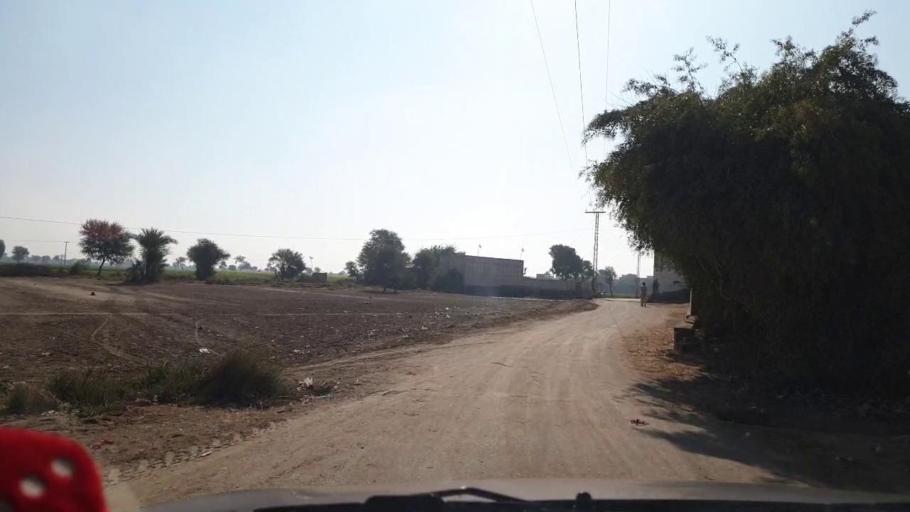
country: PK
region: Sindh
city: Sinjhoro
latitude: 25.9693
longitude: 68.7445
